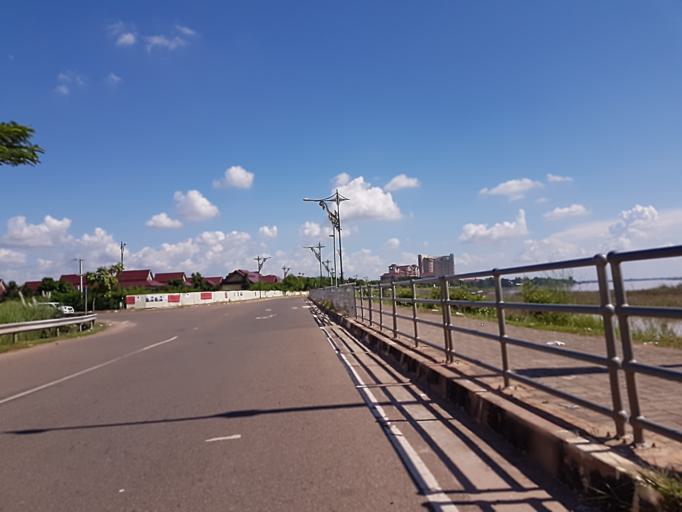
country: LA
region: Vientiane
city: Vientiane
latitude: 17.9526
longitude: 102.6140
